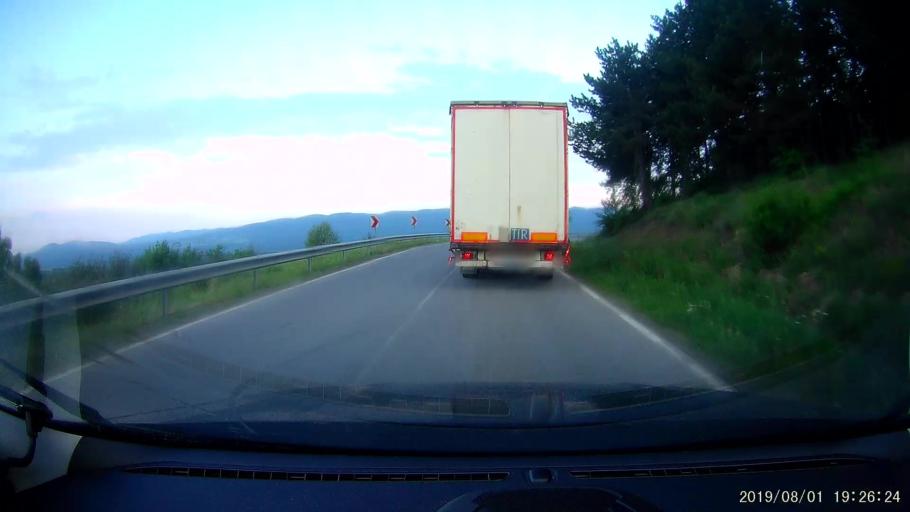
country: BG
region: Burgas
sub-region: Obshtina Sungurlare
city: Sungurlare
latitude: 42.8577
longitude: 26.9402
